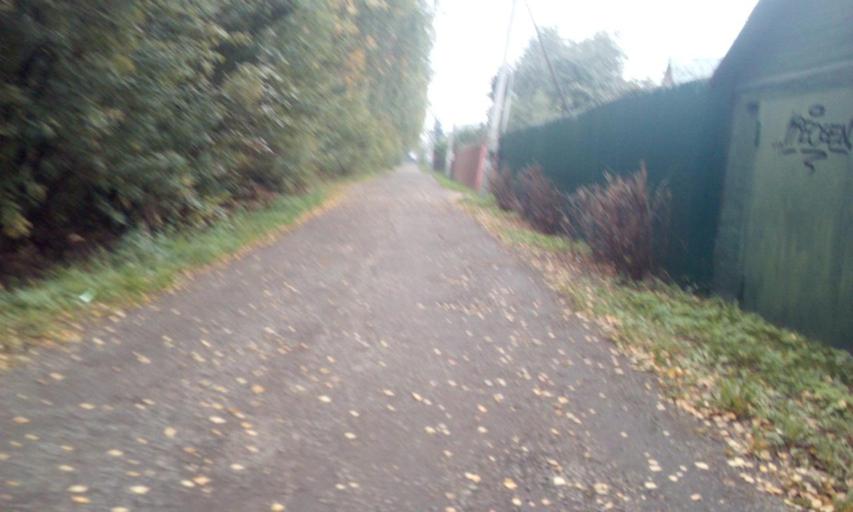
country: RU
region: Moskovskaya
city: Zhavoronki
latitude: 55.6496
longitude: 37.1148
